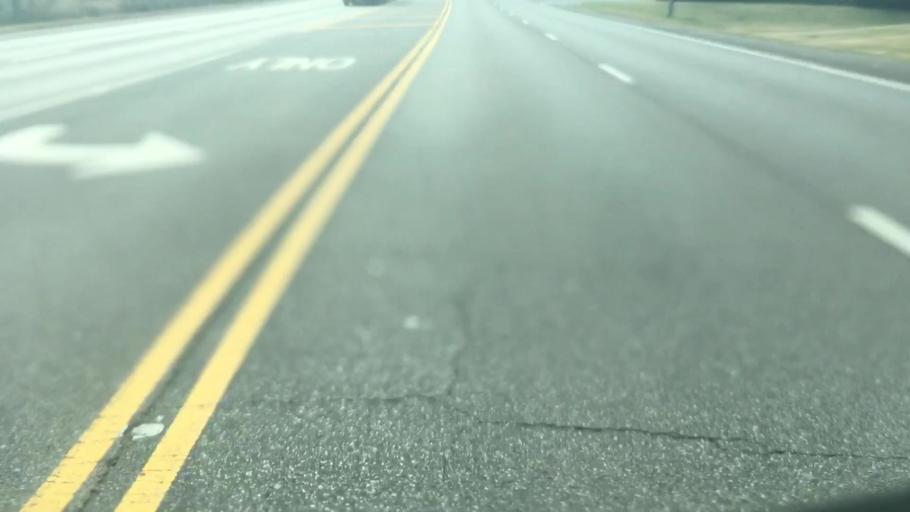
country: US
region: Alabama
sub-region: Walker County
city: Jasper
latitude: 33.8181
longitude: -87.2336
